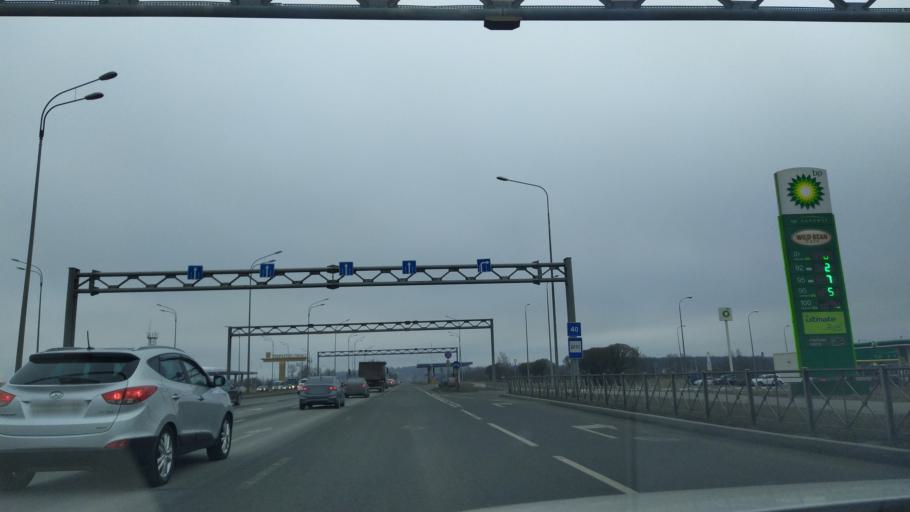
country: RU
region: St.-Petersburg
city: Shushary
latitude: 59.8032
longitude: 30.3237
